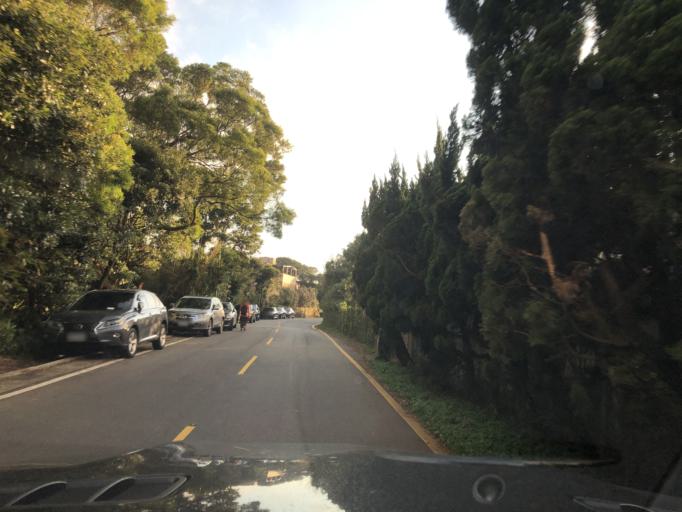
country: TW
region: Taipei
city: Taipei
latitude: 25.1509
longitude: 121.5616
